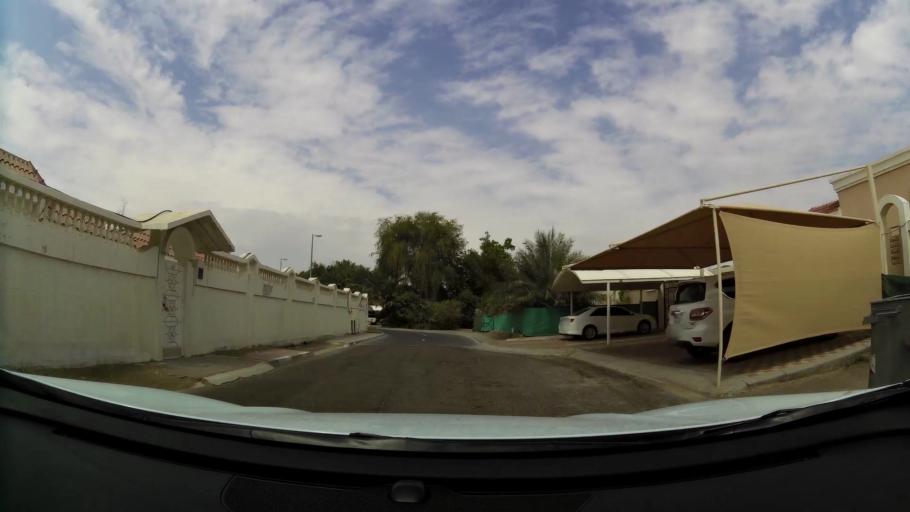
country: AE
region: Abu Dhabi
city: Al Ain
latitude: 24.1968
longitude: 55.7900
